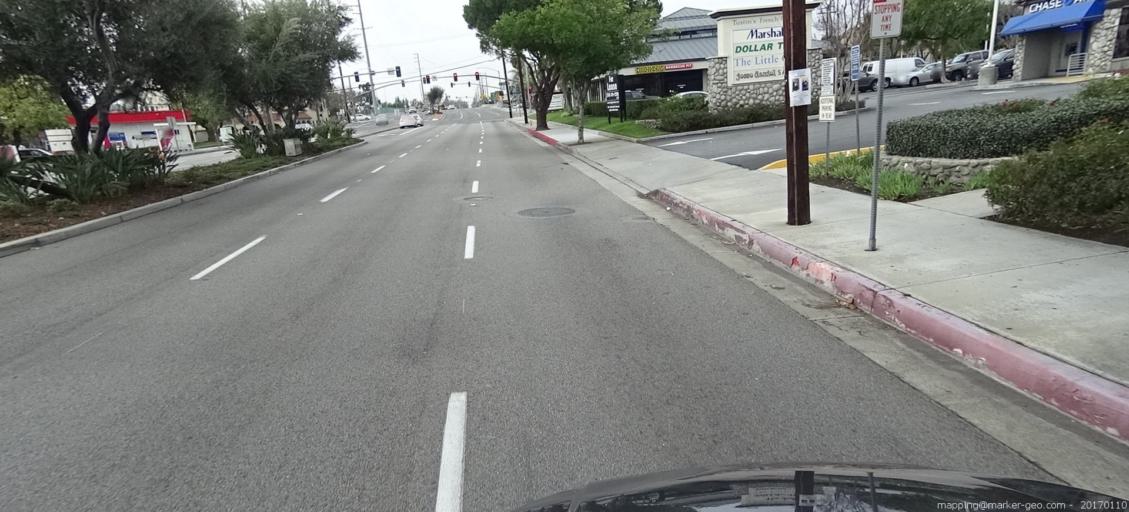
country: US
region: California
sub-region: Orange County
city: Tustin
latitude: 33.7599
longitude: -117.8279
